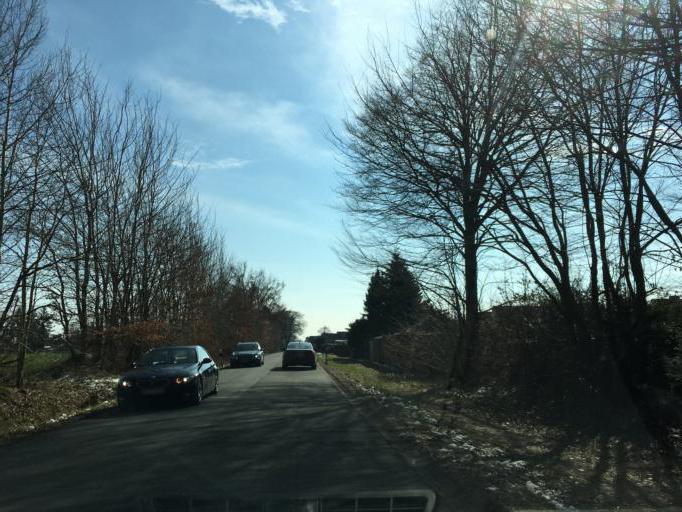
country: DE
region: Schleswig-Holstein
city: Kroppelshagen-Fahrendorf
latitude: 53.4968
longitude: 10.3187
